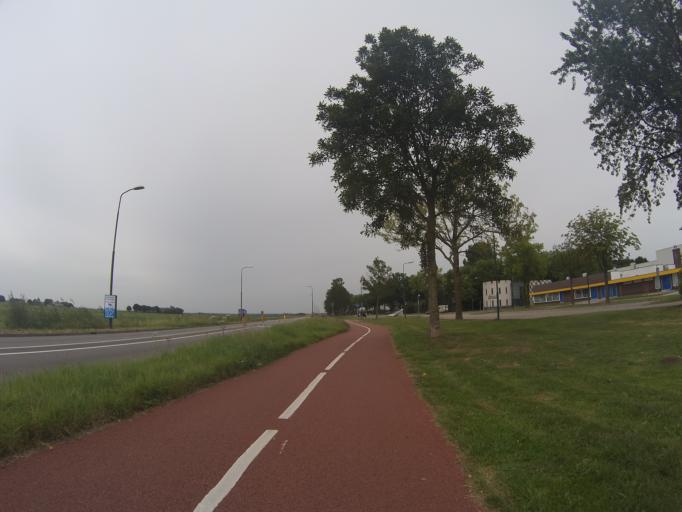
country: NL
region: Utrecht
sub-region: Gemeente Bunschoten
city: Spakenburg
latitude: 52.2443
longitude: 5.3605
